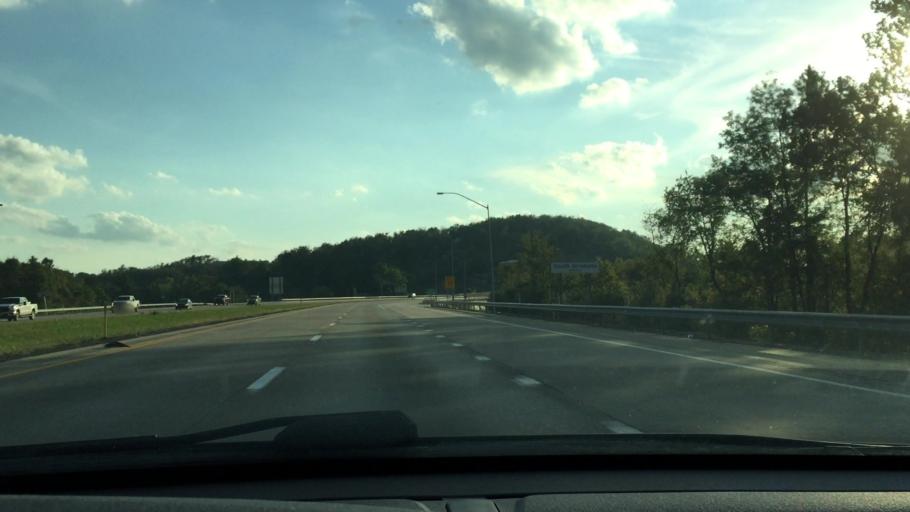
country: US
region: Pennsylvania
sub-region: Washington County
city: McGovern
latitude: 40.2126
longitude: -80.2197
